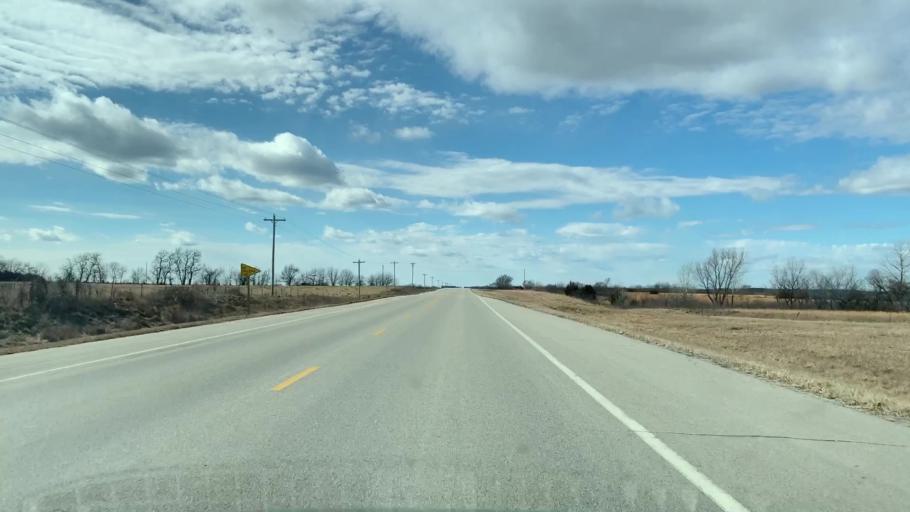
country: US
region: Kansas
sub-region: Neosho County
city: Erie
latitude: 37.5291
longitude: -95.3799
